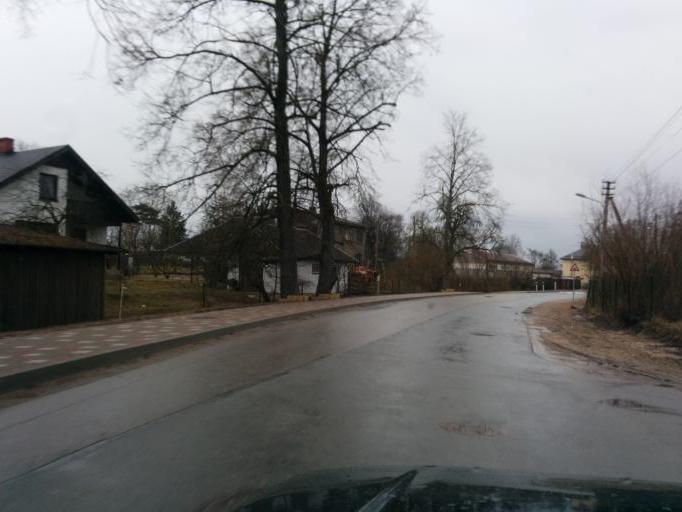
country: LV
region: Kekava
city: Kekava
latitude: 56.8722
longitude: 24.1855
